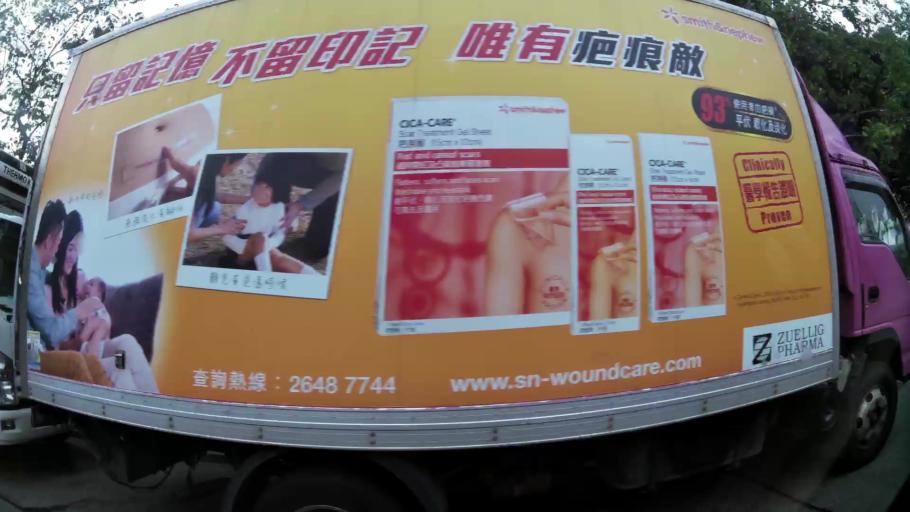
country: HK
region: Wanchai
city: Wan Chai
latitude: 22.2742
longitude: 114.1882
